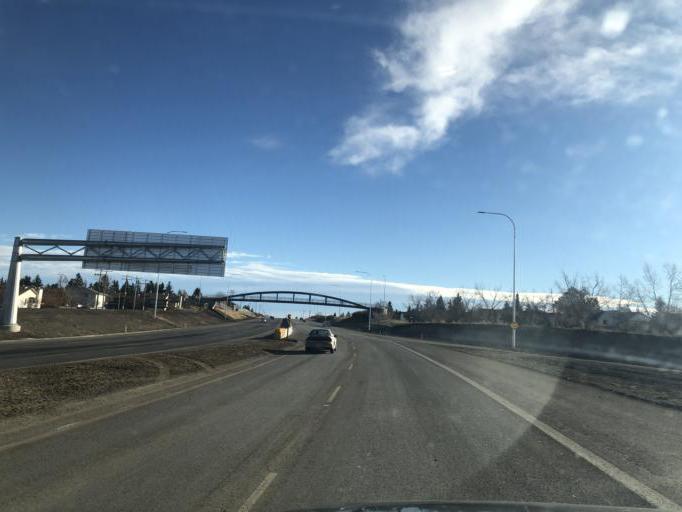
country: CA
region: Alberta
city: Calgary
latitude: 50.9505
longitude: -114.1350
